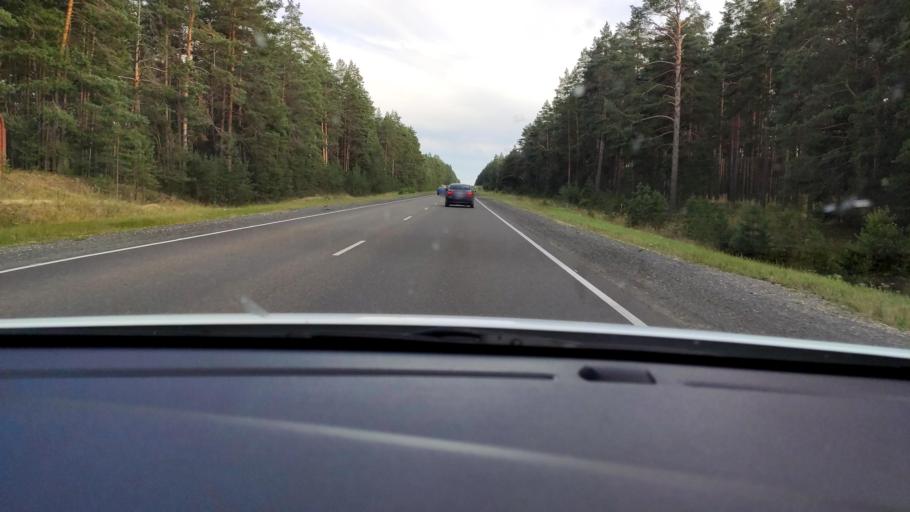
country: RU
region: Mariy-El
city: Suslonger
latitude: 56.3721
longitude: 48.2100
